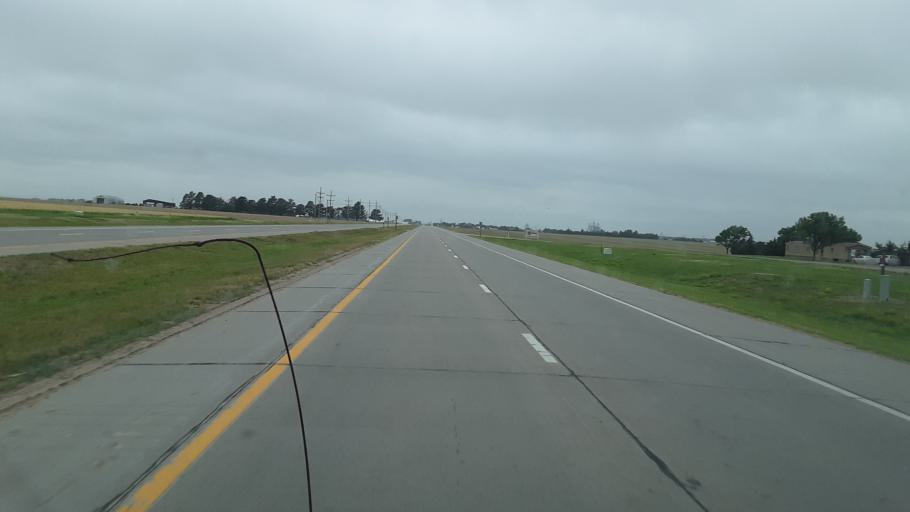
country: US
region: Kansas
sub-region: Logan County
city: Oakley
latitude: 39.1195
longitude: -100.8191
